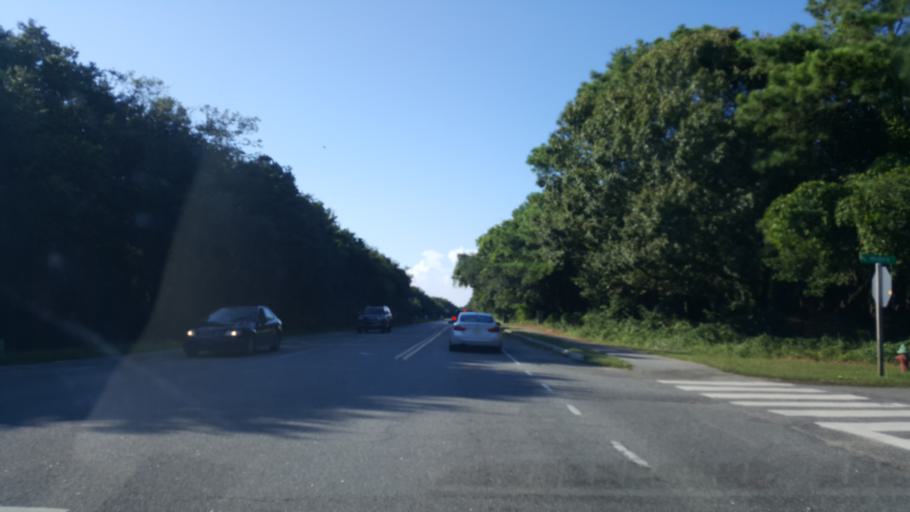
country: US
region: North Carolina
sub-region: Dare County
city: Southern Shores
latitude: 36.1348
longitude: -75.7351
